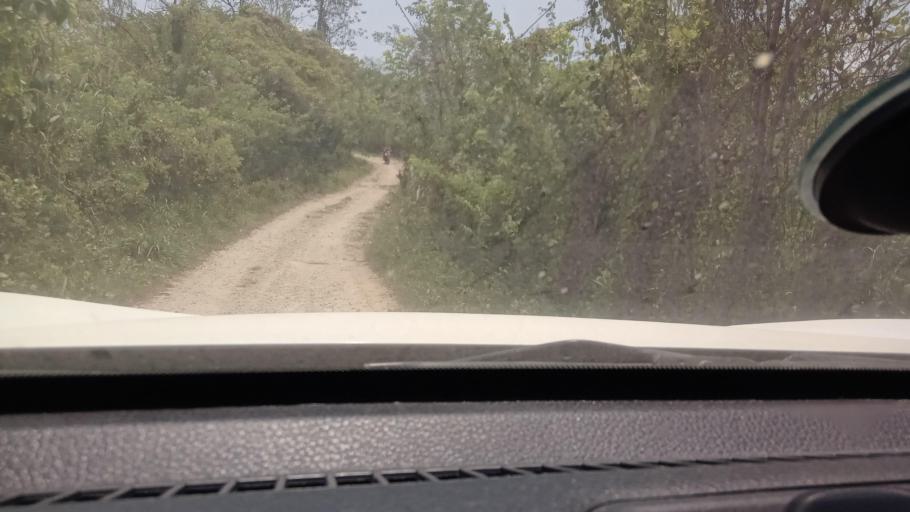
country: MX
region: Tabasco
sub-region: Huimanguillo
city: Francisco Rueda
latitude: 17.4849
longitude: -93.9398
